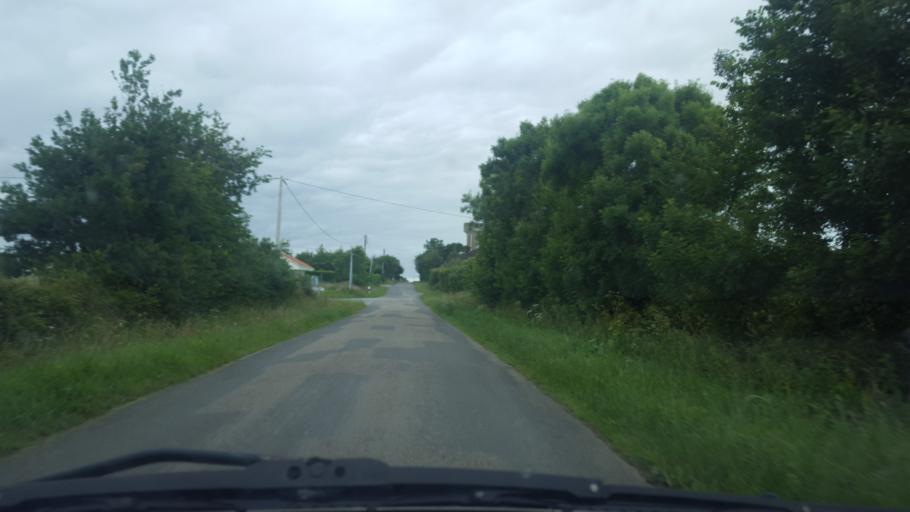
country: FR
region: Pays de la Loire
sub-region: Departement de la Loire-Atlantique
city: Saint-Philbert-de-Grand-Lieu
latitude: 47.0138
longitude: -1.6719
